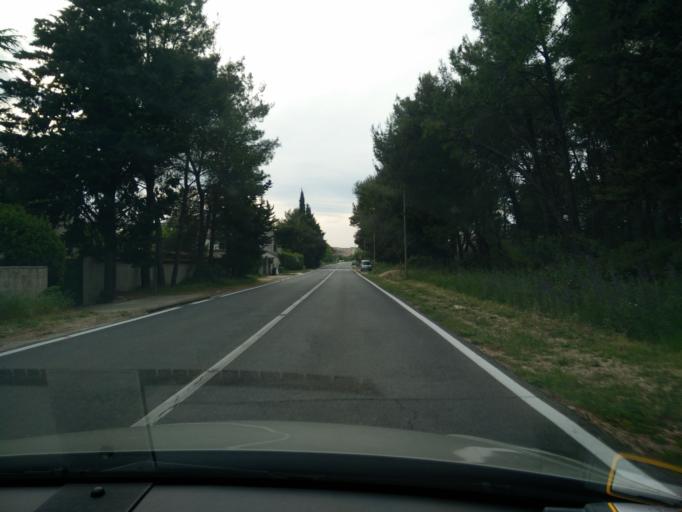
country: HR
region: Zadarska
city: Turanj
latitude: 43.9714
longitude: 15.4053
